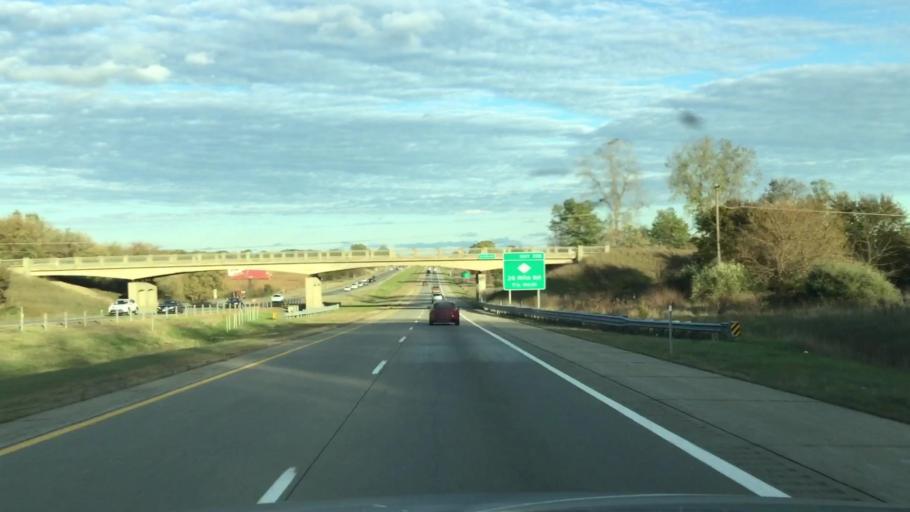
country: US
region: Michigan
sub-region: Calhoun County
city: Albion
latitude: 42.2833
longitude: -84.8295
